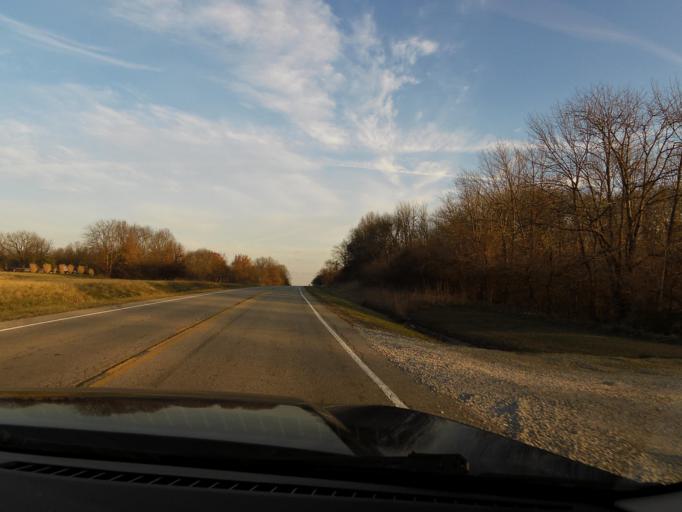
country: US
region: Illinois
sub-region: Fayette County
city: Vandalia
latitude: 38.8217
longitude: -89.0880
